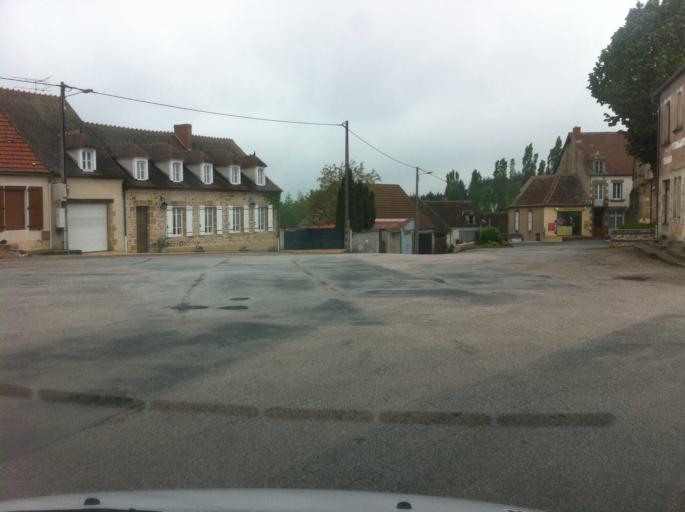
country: FR
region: Auvergne
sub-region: Departement de l'Allier
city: Montmarault
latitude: 46.3289
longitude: 3.0608
